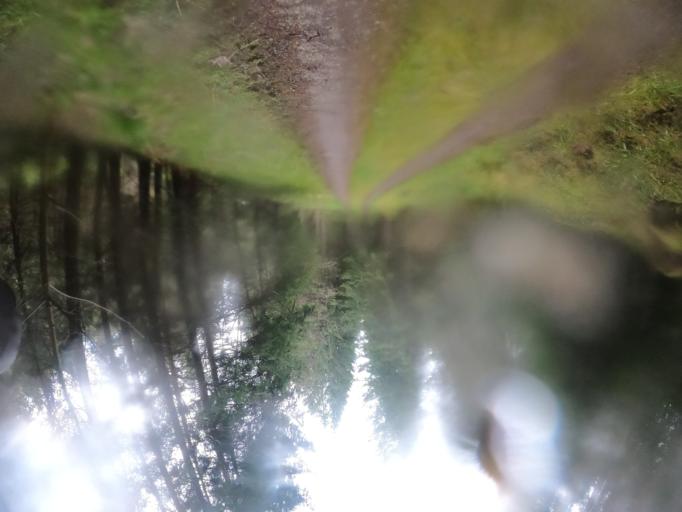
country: DE
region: Baden-Wuerttemberg
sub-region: Karlsruhe Region
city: Neuweiler
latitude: 48.6856
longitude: 8.5786
